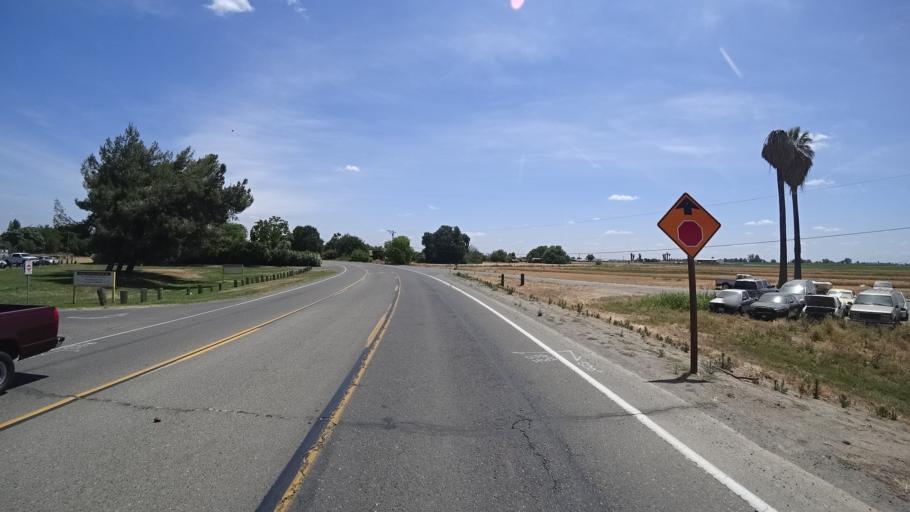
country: US
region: California
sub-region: Kings County
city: Lemoore
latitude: 36.2986
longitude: -119.7667
